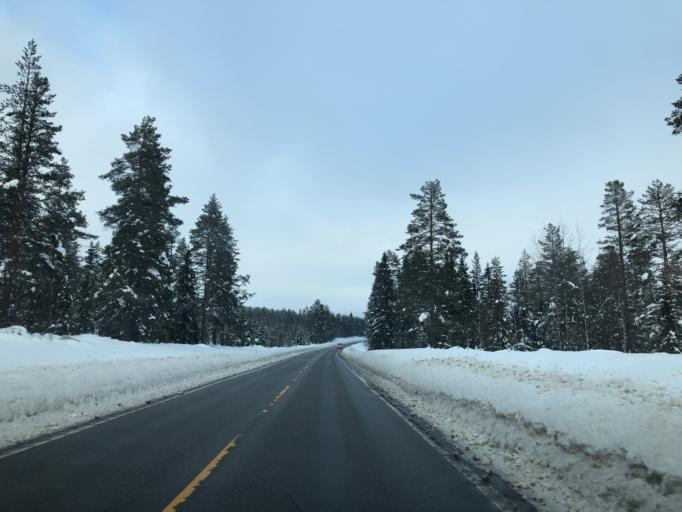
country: NO
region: Hedmark
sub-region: Trysil
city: Innbygda
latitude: 61.2230
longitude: 12.2449
